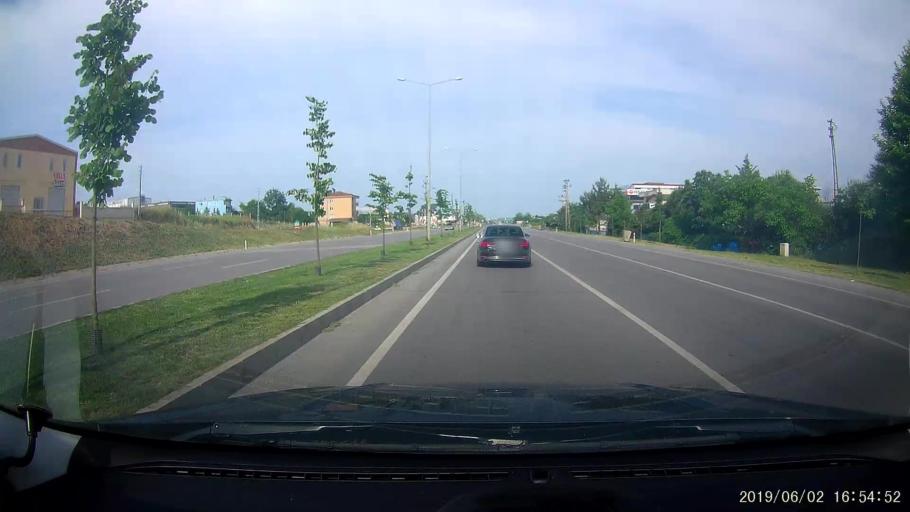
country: TR
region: Samsun
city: Samsun
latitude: 41.2920
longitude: 36.2407
